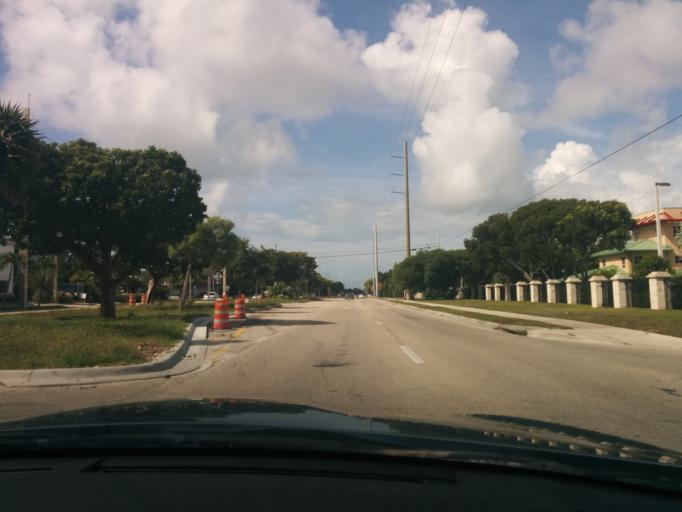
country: US
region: Florida
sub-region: Monroe County
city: Tavernier
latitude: 25.0077
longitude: -80.5189
